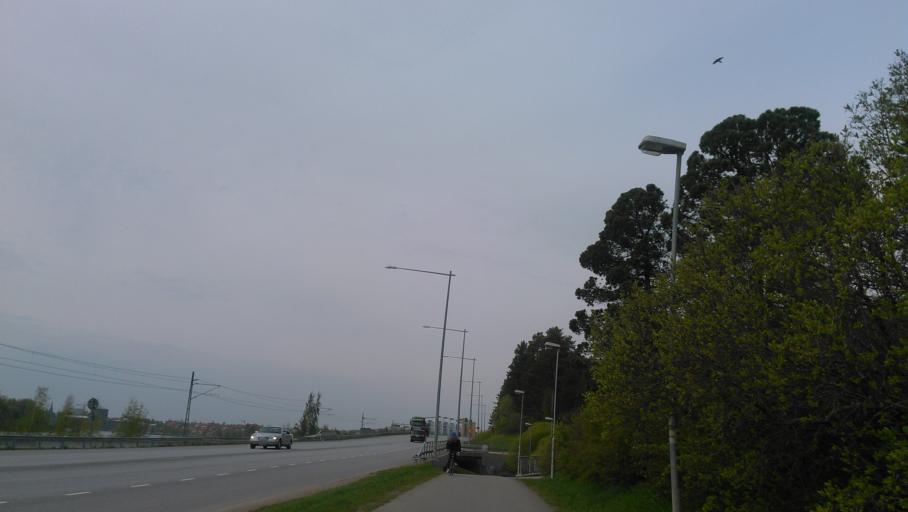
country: SE
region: Vaesterbotten
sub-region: Umea Kommun
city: Umea
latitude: 63.8082
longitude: 20.2974
